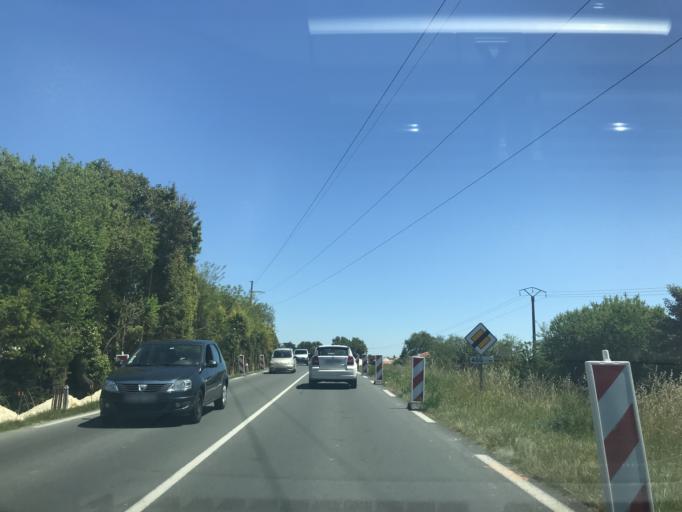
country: FR
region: Poitou-Charentes
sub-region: Departement de la Charente-Maritime
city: Royan
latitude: 45.6407
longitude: -1.0330
